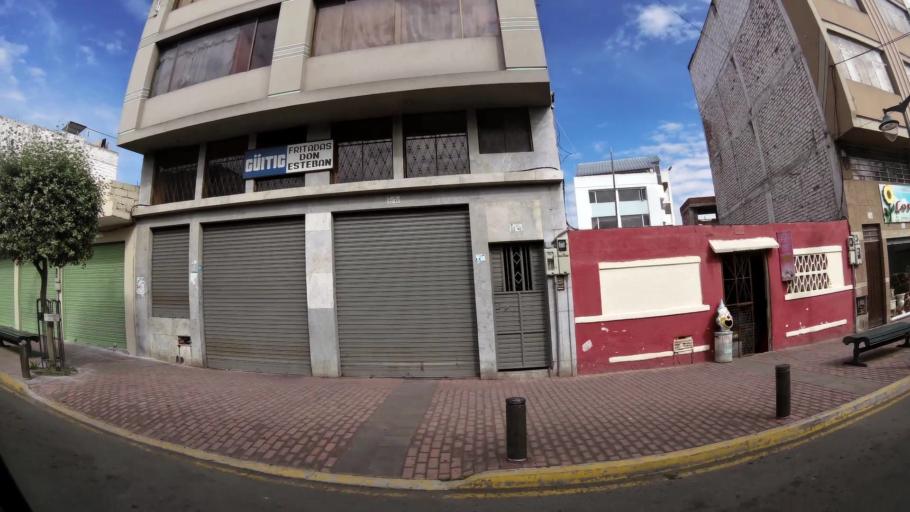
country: EC
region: Tungurahua
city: Ambato
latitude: -1.2312
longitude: -78.6296
